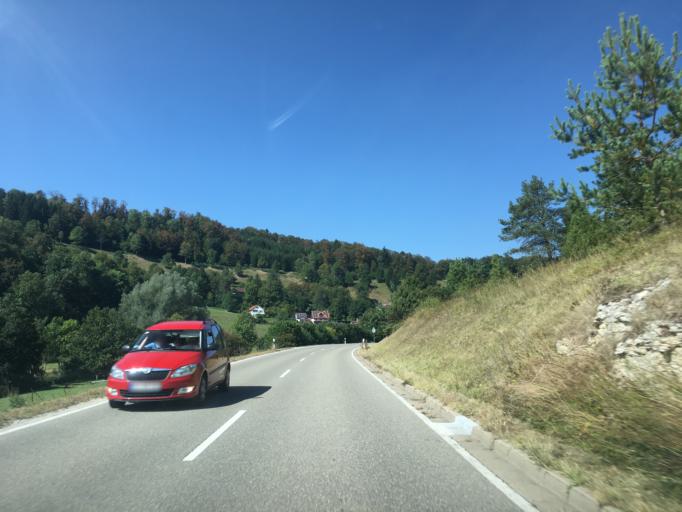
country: DE
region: Baden-Wuerttemberg
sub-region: Tuebingen Region
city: Hayingen
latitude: 48.3283
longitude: 9.4997
